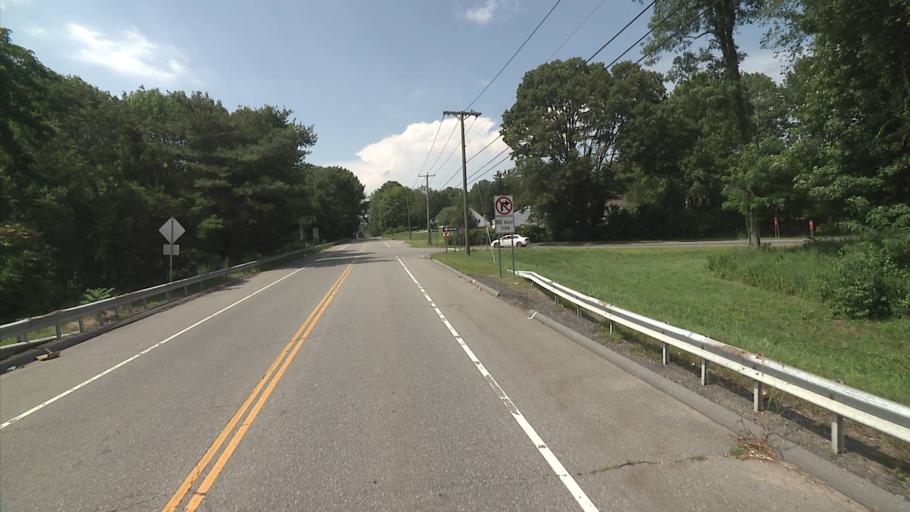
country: US
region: Connecticut
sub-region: New London County
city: Colchester
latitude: 41.5630
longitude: -72.3171
